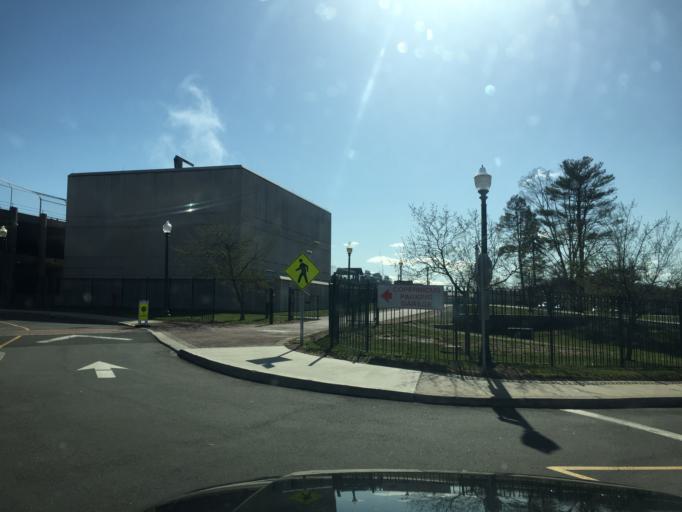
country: US
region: Connecticut
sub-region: Hartford County
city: New Britain
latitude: 41.6926
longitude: -72.7625
